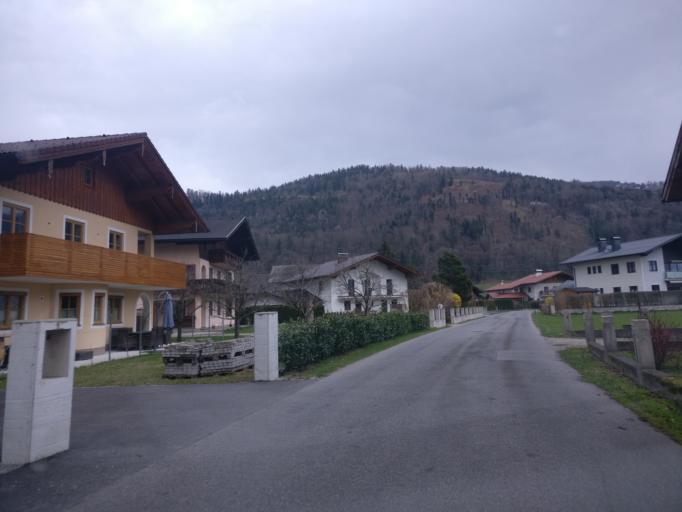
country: AT
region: Salzburg
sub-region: Politischer Bezirk Hallein
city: Kuchl
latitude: 47.6303
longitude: 13.1658
